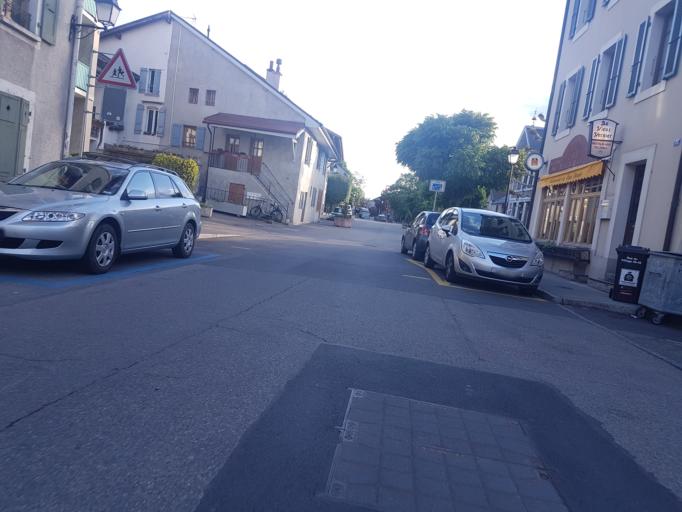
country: CH
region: Geneva
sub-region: Geneva
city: Vernier
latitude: 46.2138
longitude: 6.0823
